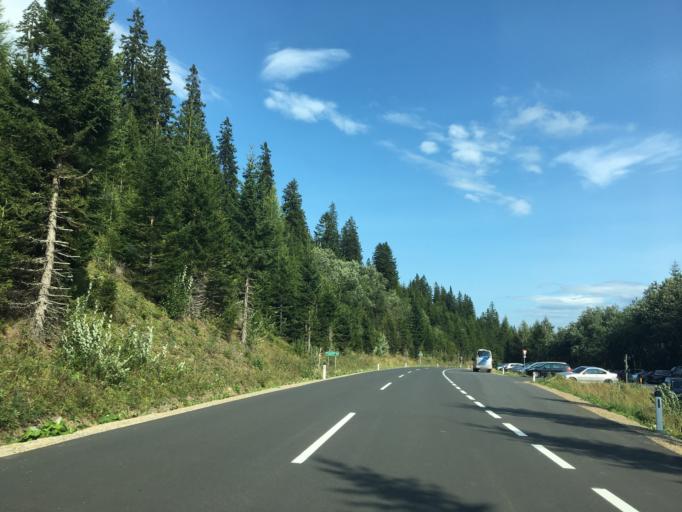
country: AT
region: Styria
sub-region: Politischer Bezirk Deutschlandsberg
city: Kloster
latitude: 46.8292
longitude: 15.0142
